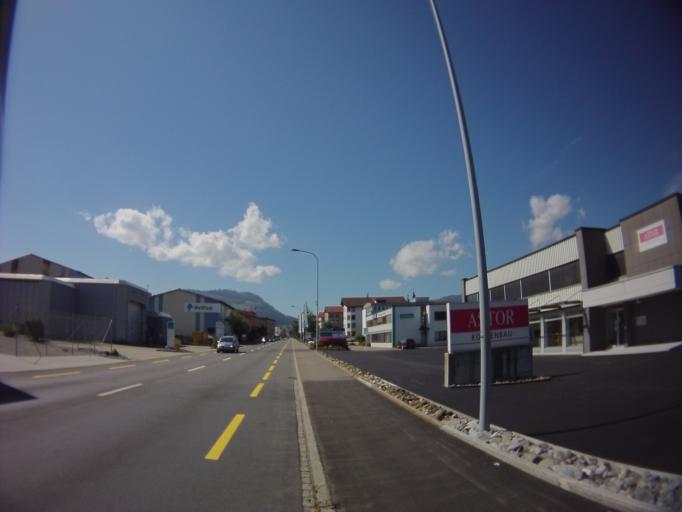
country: CH
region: Schwyz
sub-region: Bezirk Einsiedeln
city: Einsiedeln
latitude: 47.1354
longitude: 8.7452
